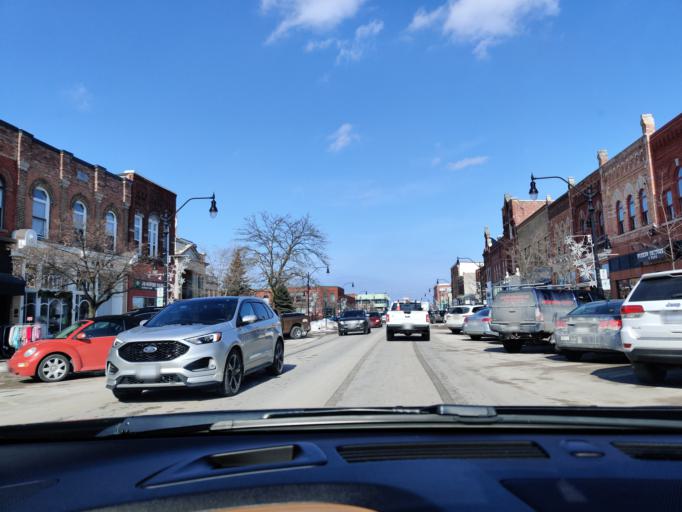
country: CA
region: Ontario
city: Collingwood
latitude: 44.5010
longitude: -80.2170
